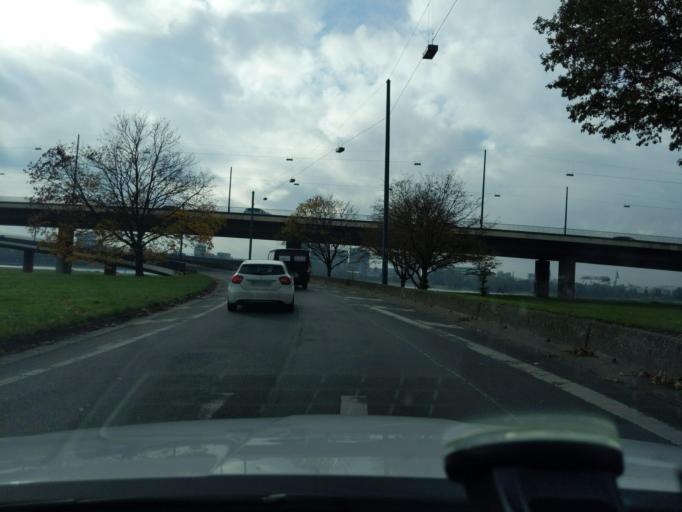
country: DE
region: North Rhine-Westphalia
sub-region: Regierungsbezirk Dusseldorf
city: Dusseldorf
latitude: 51.2262
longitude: 6.7583
